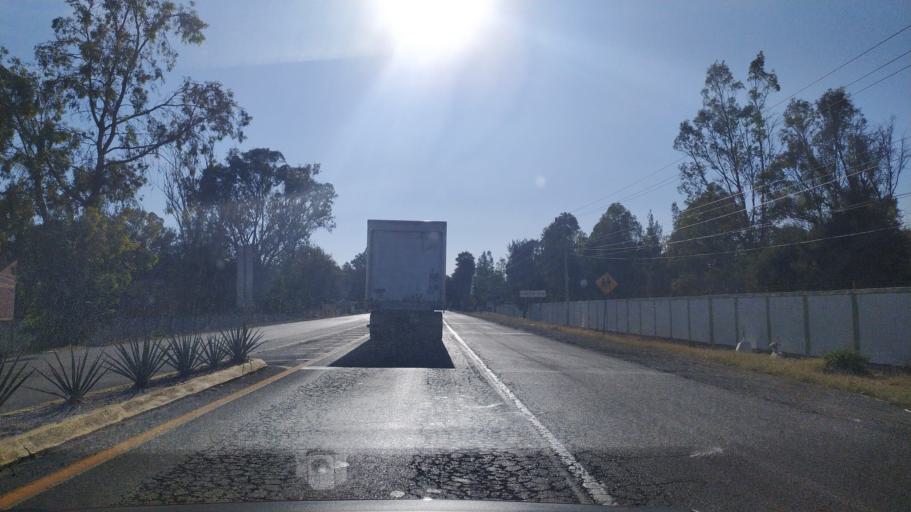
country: MX
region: Jalisco
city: Jamay
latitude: 20.2942
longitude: -102.6745
